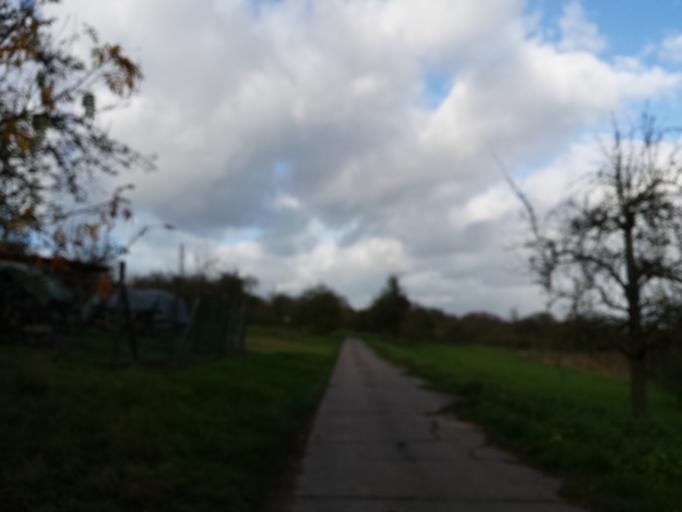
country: DE
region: Hesse
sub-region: Regierungsbezirk Darmstadt
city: Bad Nauheim
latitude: 50.3371
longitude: 8.7164
